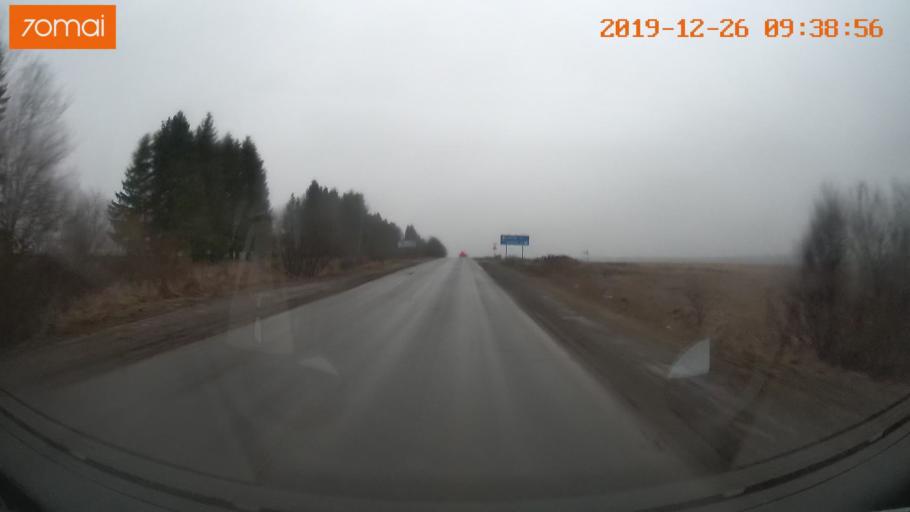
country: RU
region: Vologda
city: Vologda
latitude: 59.1494
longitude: 40.0337
